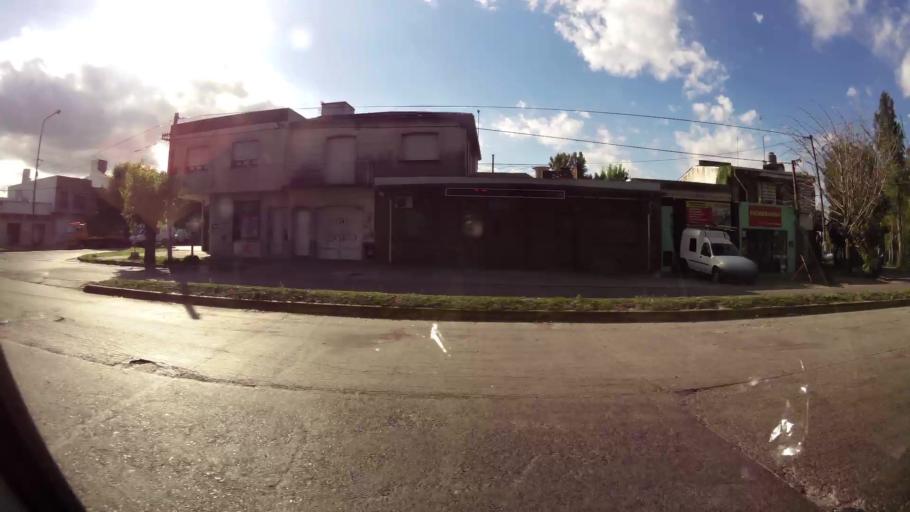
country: AR
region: Buenos Aires
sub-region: Partido de La Plata
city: La Plata
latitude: -34.8883
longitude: -57.9575
